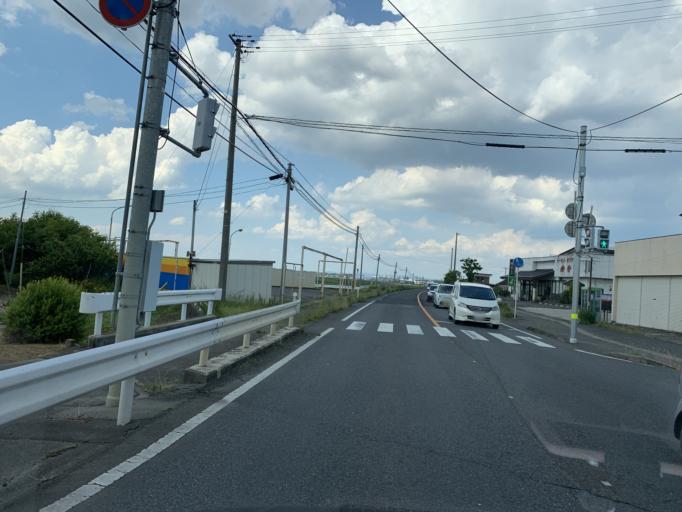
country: JP
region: Miyagi
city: Wakuya
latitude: 38.6183
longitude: 141.1803
